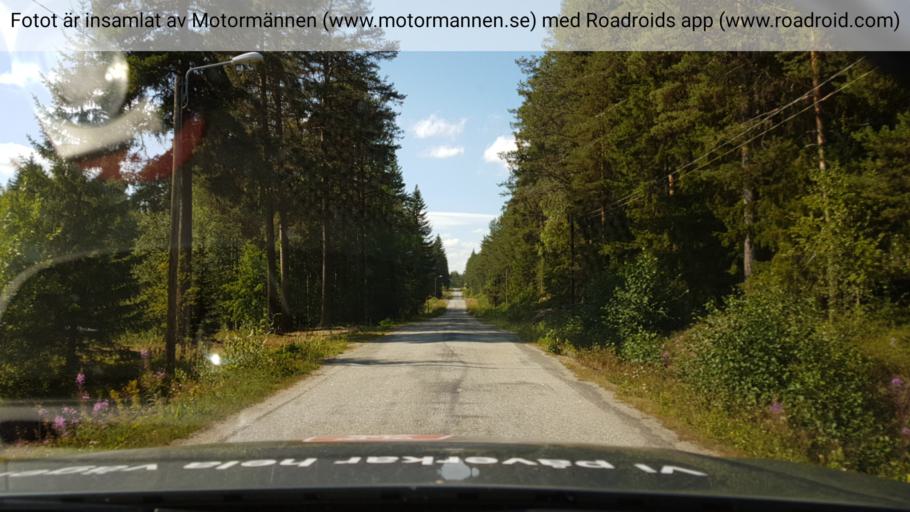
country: SE
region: Vaesterbotten
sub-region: Dorotea Kommun
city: Dorotea
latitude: 64.0992
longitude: 16.4097
